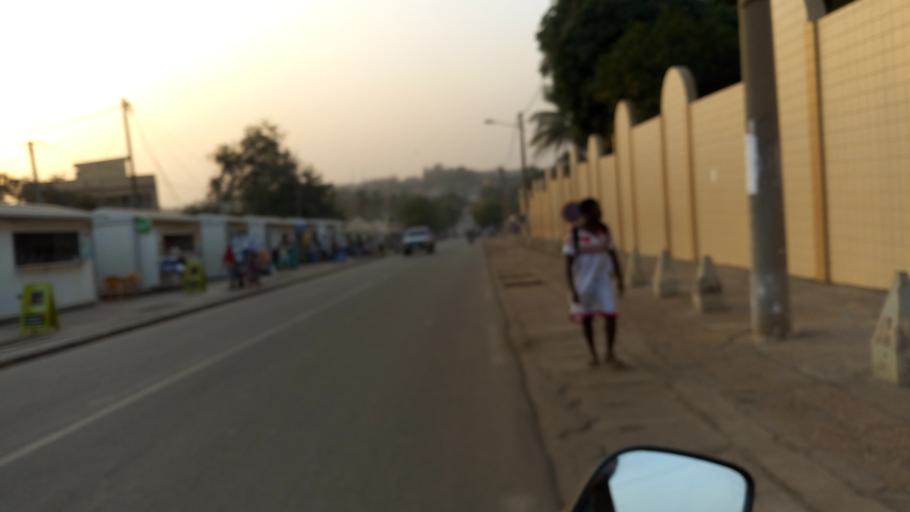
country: TG
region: Kara
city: Kara
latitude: 9.5480
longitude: 1.1898
